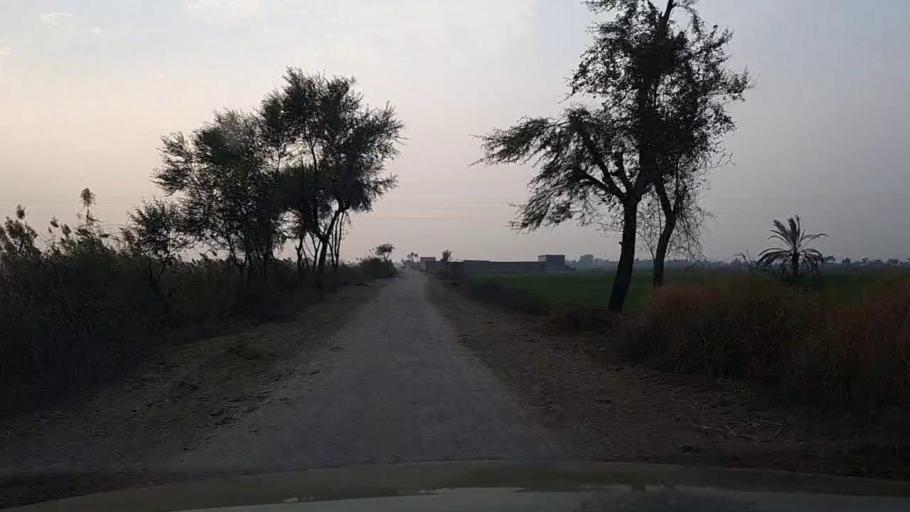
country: PK
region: Sindh
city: Sanghar
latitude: 26.1857
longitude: 68.9529
